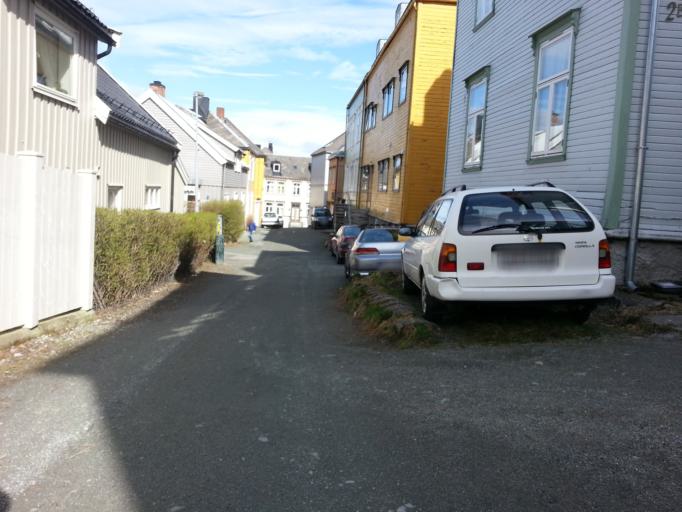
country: NO
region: Sor-Trondelag
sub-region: Trondheim
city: Trondheim
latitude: 63.4303
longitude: 10.4137
